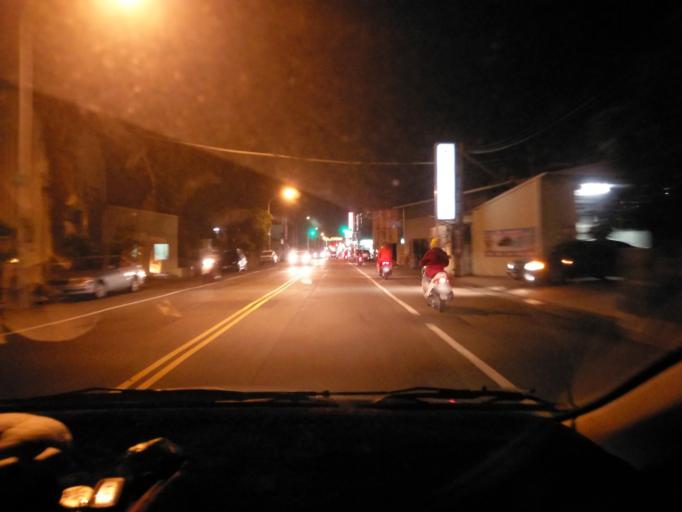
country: TW
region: Taiwan
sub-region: Miaoli
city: Miaoli
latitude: 24.6937
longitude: 120.8708
